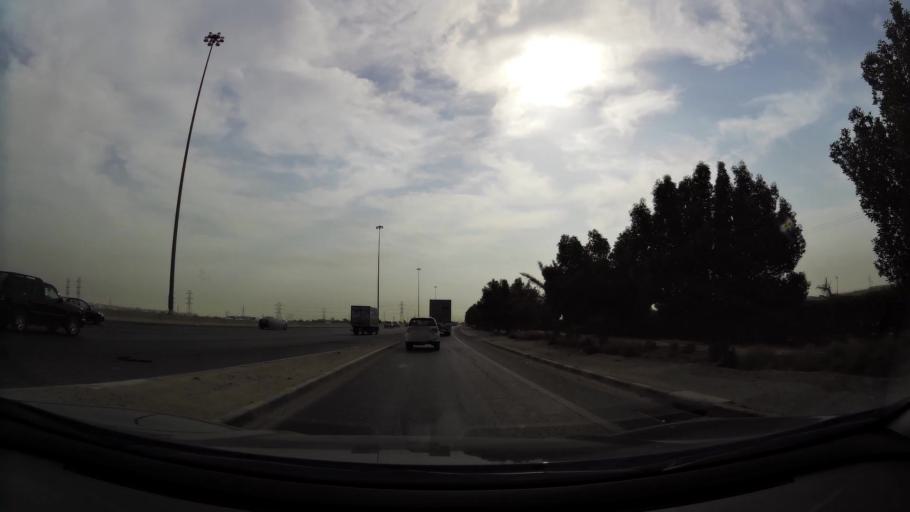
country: KW
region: Muhafazat al Jahra'
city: Al Jahra'
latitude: 29.3213
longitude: 47.7554
